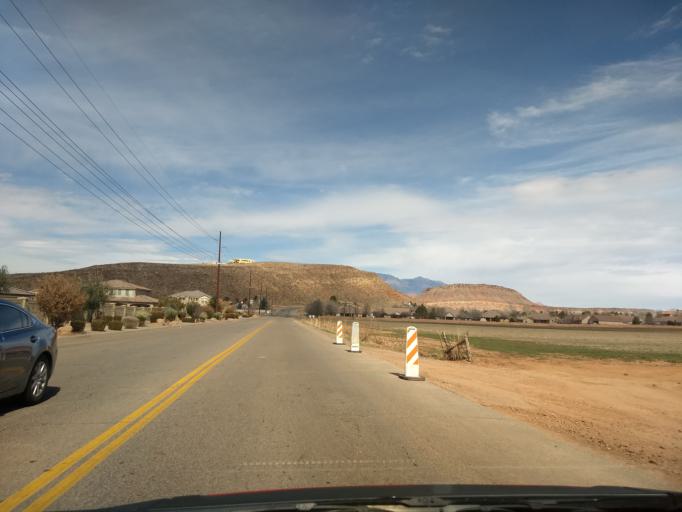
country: US
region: Utah
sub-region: Washington County
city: Washington
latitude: 37.0915
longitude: -113.4998
